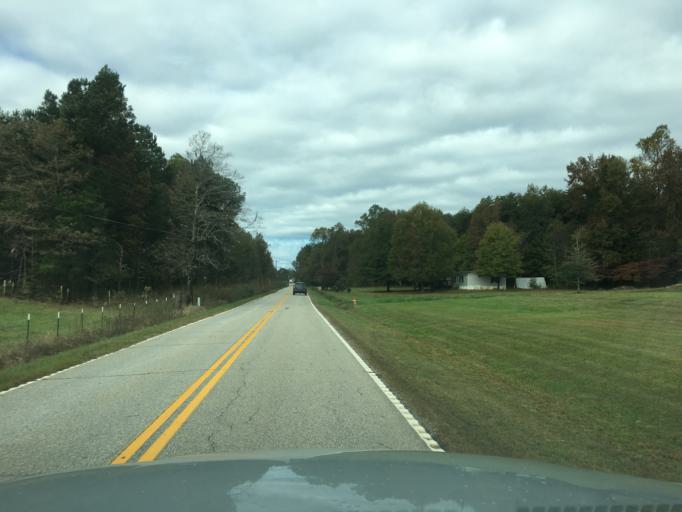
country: US
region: South Carolina
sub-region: Greenville County
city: Tigerville
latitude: 35.0595
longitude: -82.2644
